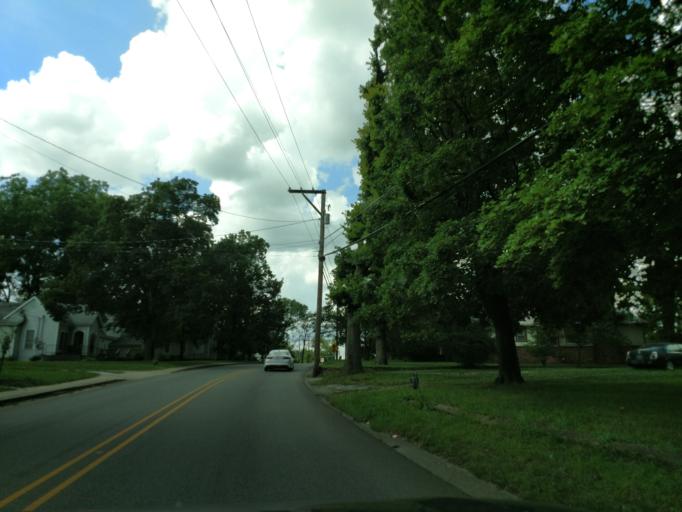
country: US
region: Arkansas
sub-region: Carroll County
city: Berryville
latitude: 36.3686
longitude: -93.5671
